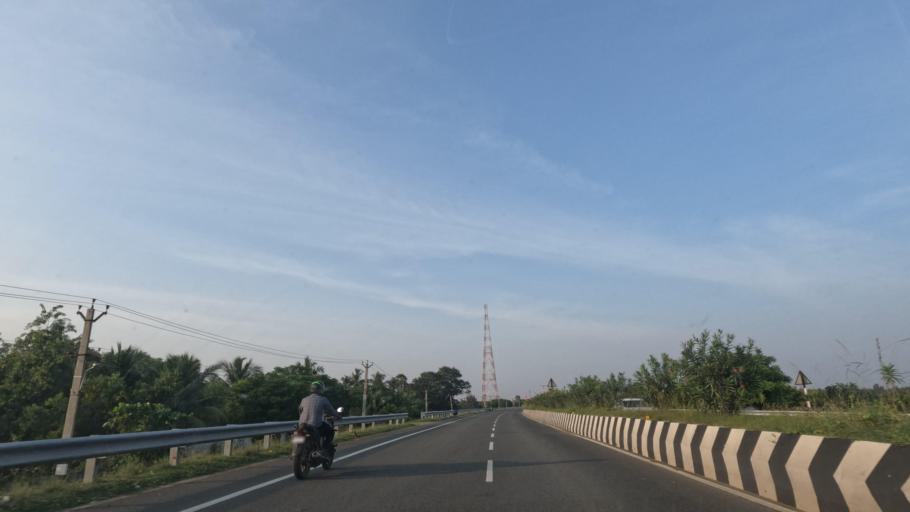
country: IN
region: Tamil Nadu
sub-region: Kancheepuram
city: Mamallapuram
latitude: 12.7071
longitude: 80.2238
